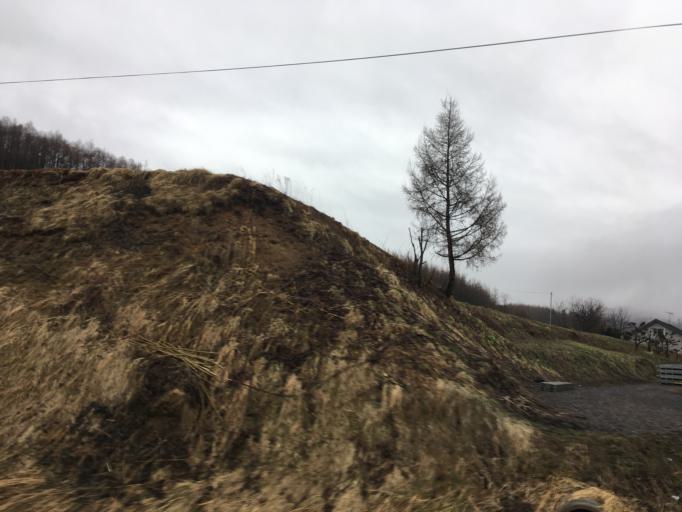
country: JP
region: Hokkaido
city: Nayoro
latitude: 44.0718
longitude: 142.4132
